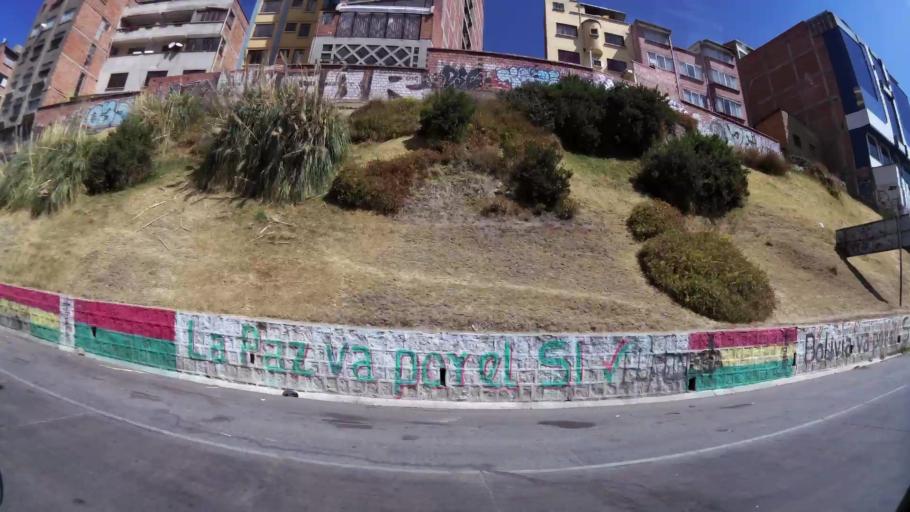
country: BO
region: La Paz
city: La Paz
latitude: -16.4864
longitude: -68.1453
